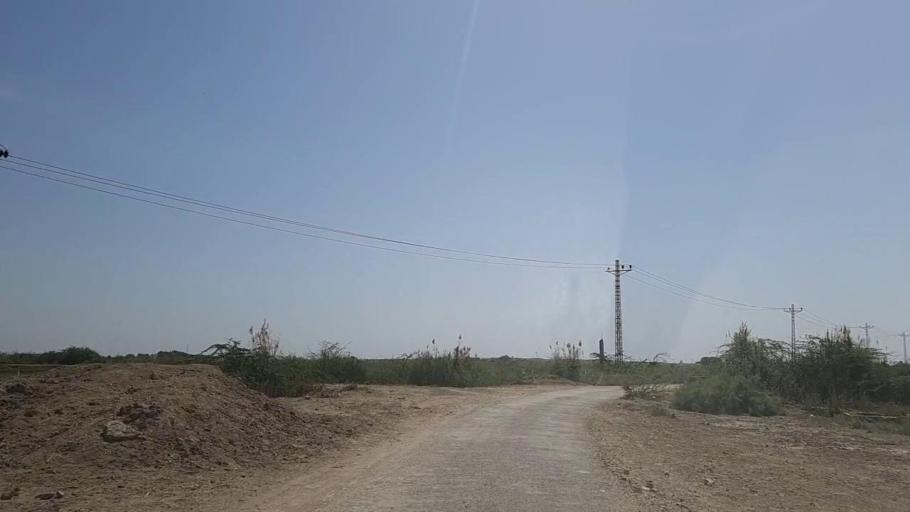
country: PK
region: Sindh
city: Gharo
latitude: 24.7681
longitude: 67.7517
